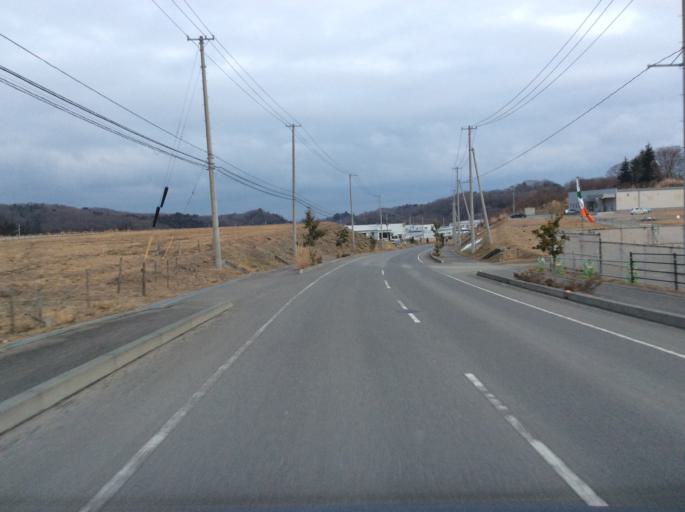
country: JP
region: Fukushima
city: Iwaki
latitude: 37.1265
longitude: 140.9718
